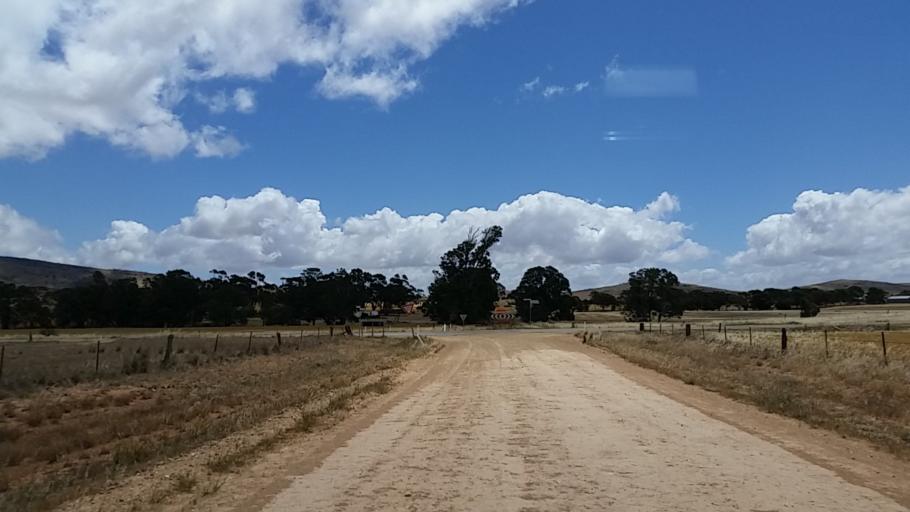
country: AU
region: South Australia
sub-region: Peterborough
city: Peterborough
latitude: -32.8493
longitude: 138.5487
